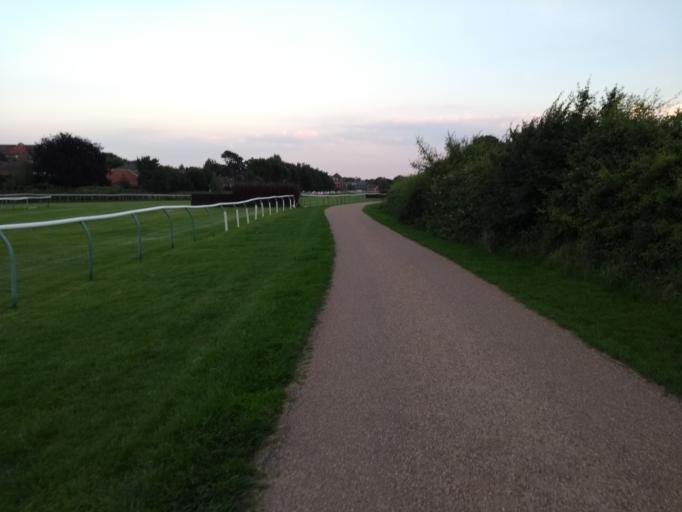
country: GB
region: England
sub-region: Warwickshire
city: Warwick
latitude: 52.2836
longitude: -1.5959
